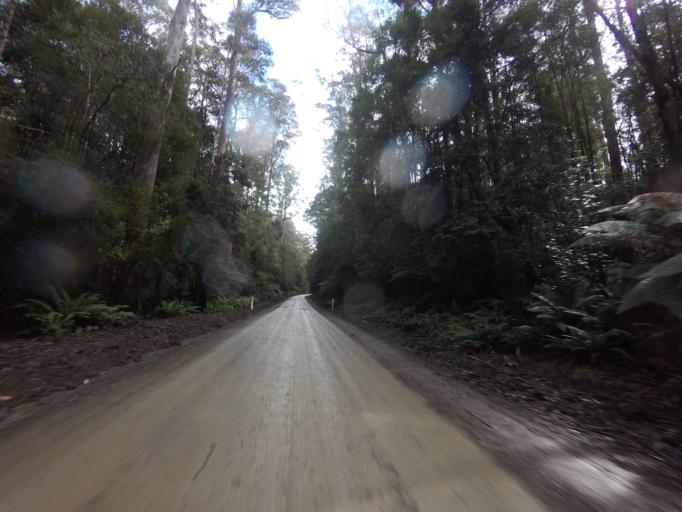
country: AU
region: Tasmania
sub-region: Huon Valley
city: Geeveston
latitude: -43.3870
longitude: 146.8481
